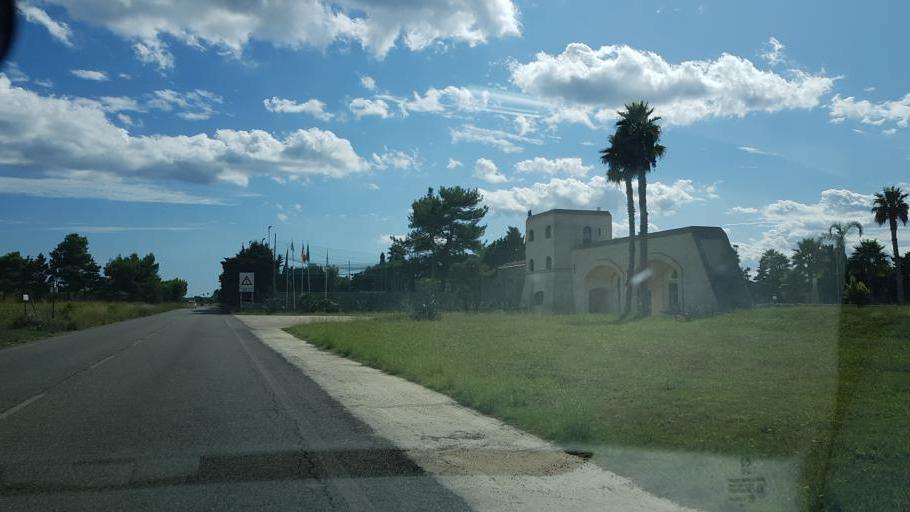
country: IT
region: Apulia
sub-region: Provincia di Lecce
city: Borgagne
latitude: 40.2621
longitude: 18.4339
